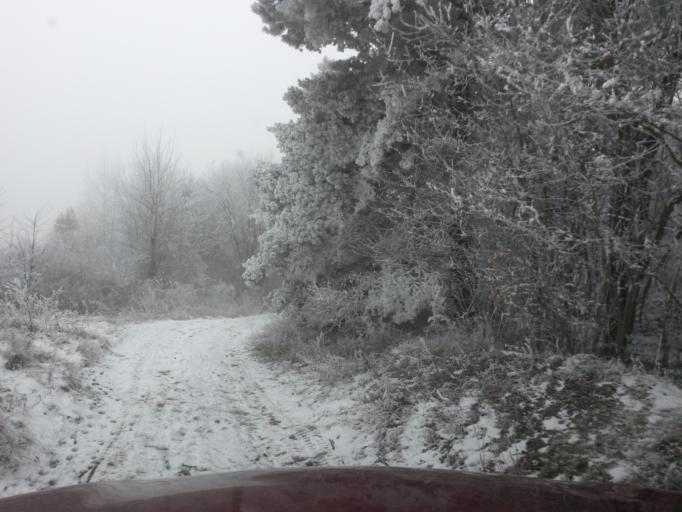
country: SK
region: Kosicky
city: Krompachy
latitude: 48.9719
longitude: 20.9805
